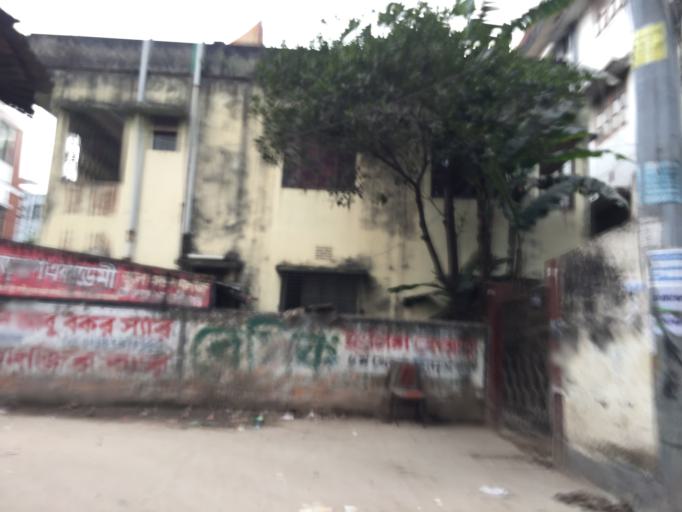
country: BD
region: Dhaka
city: Azimpur
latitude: 23.7982
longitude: 90.3632
